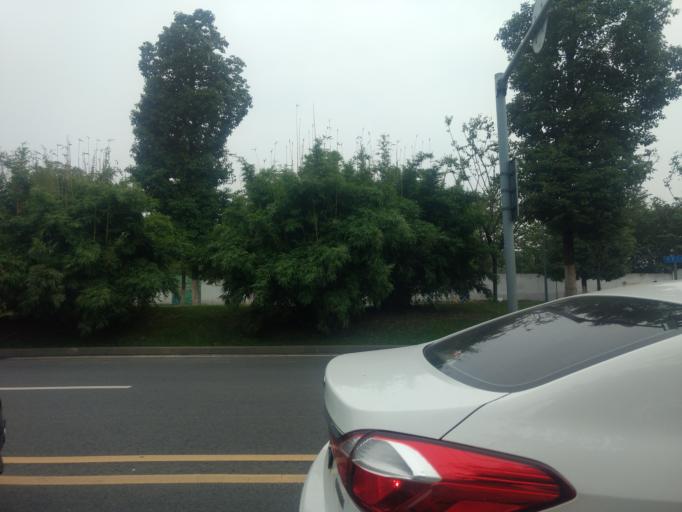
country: CN
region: Sichuan
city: Chengdu
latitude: 30.7294
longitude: 104.1363
